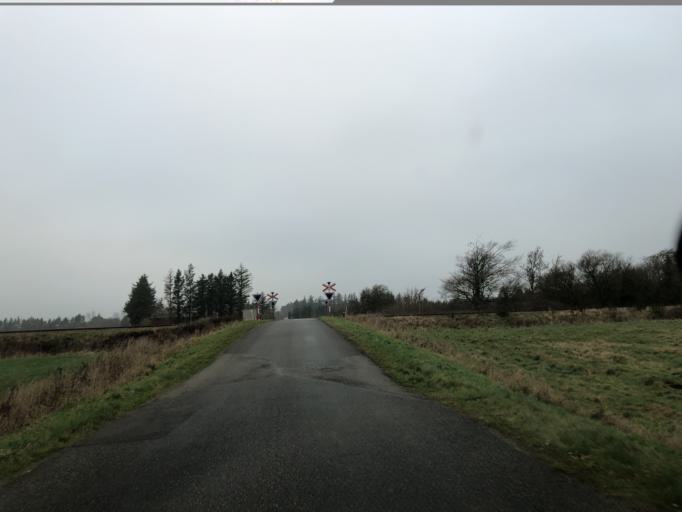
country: DK
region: Central Jutland
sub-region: Holstebro Kommune
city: Ulfborg
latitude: 56.2058
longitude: 8.3124
